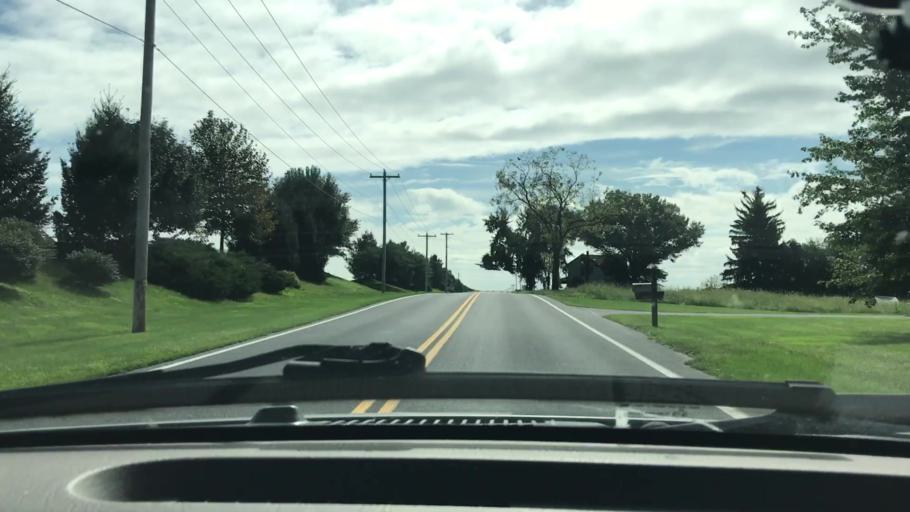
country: US
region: Pennsylvania
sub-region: Lancaster County
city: Manheim
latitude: 40.1401
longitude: -76.4066
